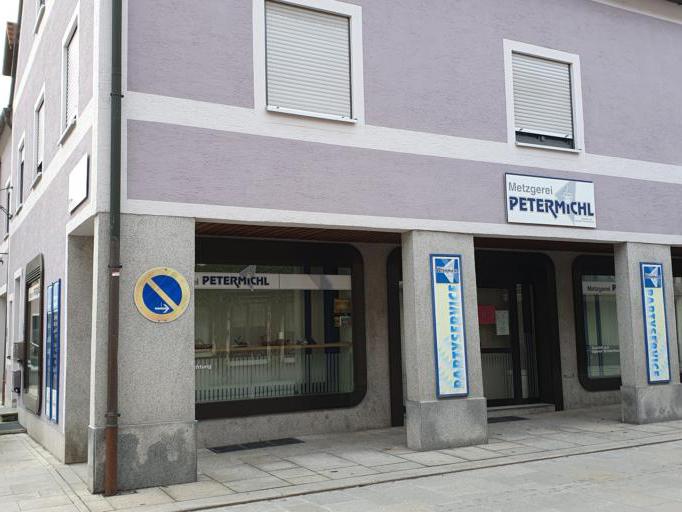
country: DE
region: Bavaria
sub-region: Upper Palatinate
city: Hemau
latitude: 49.0524
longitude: 11.7822
